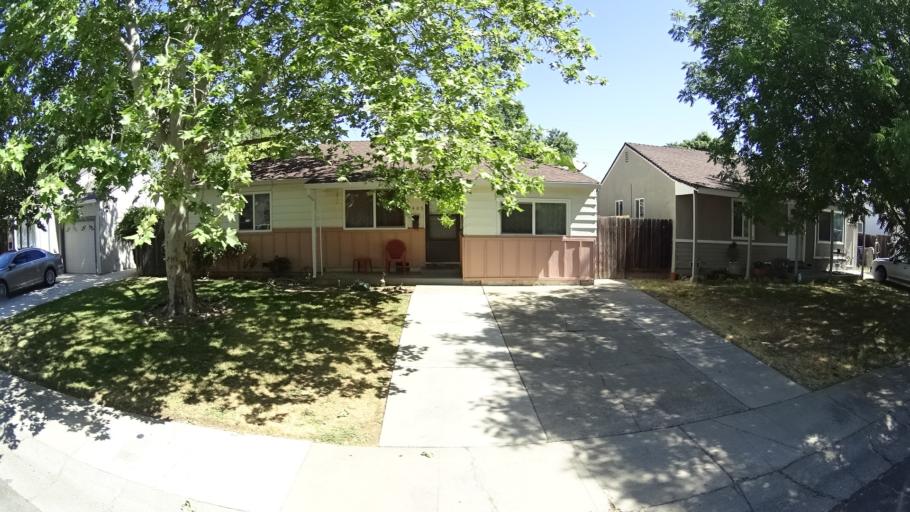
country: US
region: California
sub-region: Sacramento County
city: Parkway
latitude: 38.5197
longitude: -121.5043
